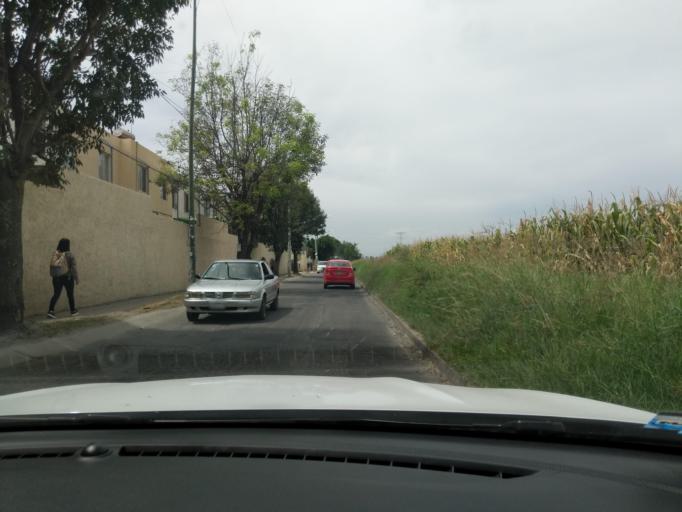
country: MX
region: Jalisco
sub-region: Zapopan
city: La Cuchilla (Extramuros de Tesistan)
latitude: 20.7804
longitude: -103.4654
